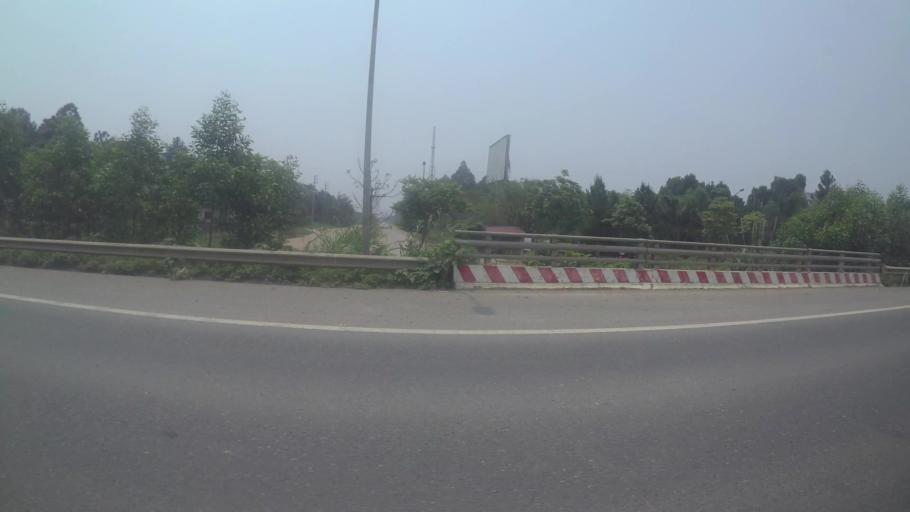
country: VN
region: Ha Noi
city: Lien Quan
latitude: 20.9899
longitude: 105.5553
